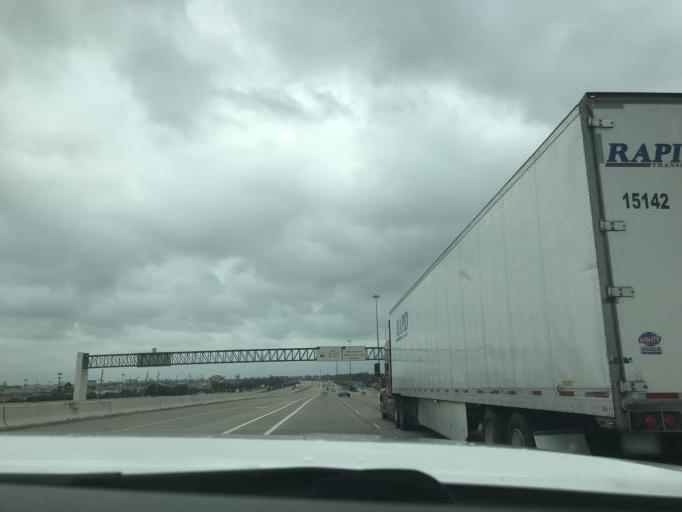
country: US
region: Texas
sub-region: Fort Bend County
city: Greatwood
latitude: 29.5616
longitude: -95.6888
